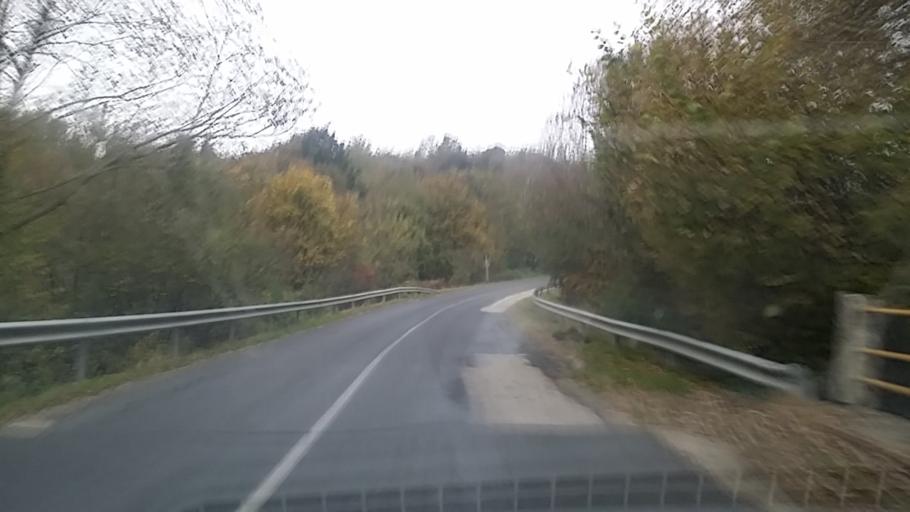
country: HU
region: Veszprem
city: Herend
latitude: 47.2507
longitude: 17.7487
